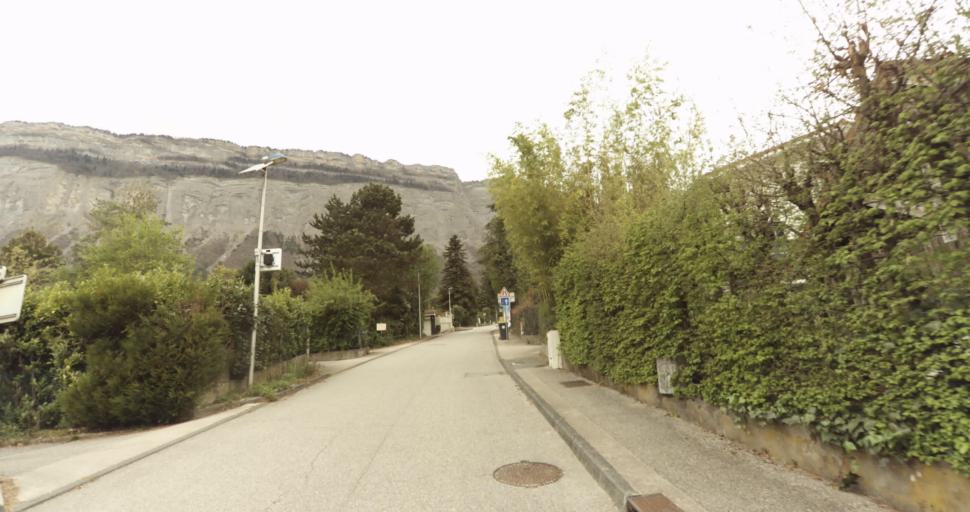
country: FR
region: Rhone-Alpes
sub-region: Departement de l'Isere
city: Biviers
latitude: 45.2291
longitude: 5.7948
